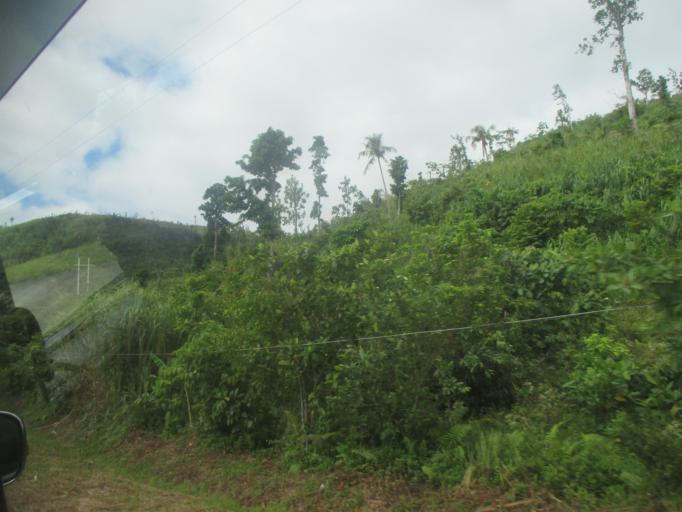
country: PH
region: Eastern Visayas
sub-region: Province of Eastern Samar
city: Lawa-an
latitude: 11.1188
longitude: 125.2448
